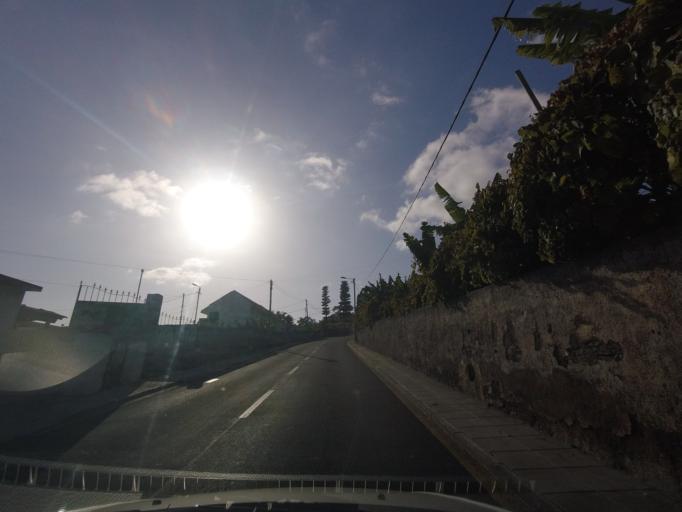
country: PT
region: Madeira
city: Camara de Lobos
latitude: 32.6558
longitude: -16.9387
